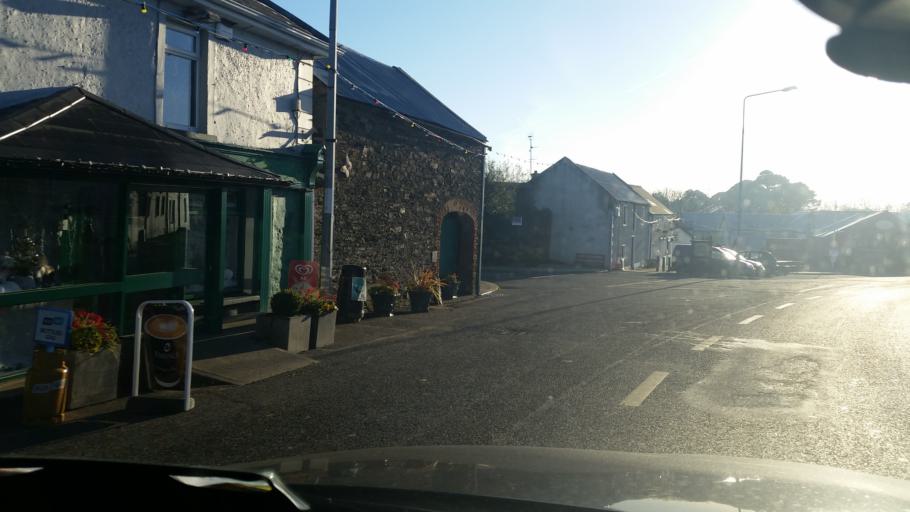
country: IE
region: Leinster
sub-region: Loch Garman
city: Gorey
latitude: 52.6099
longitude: -6.3047
